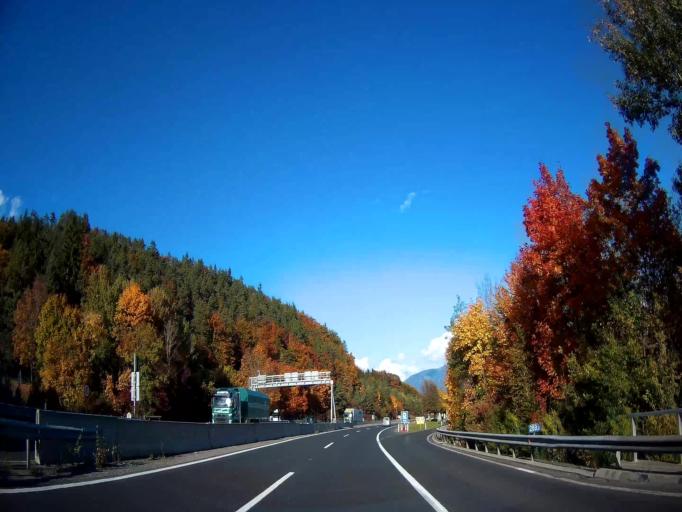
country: AT
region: Carinthia
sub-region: Politischer Bezirk Volkermarkt
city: Griffen
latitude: 46.7136
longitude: 14.7789
